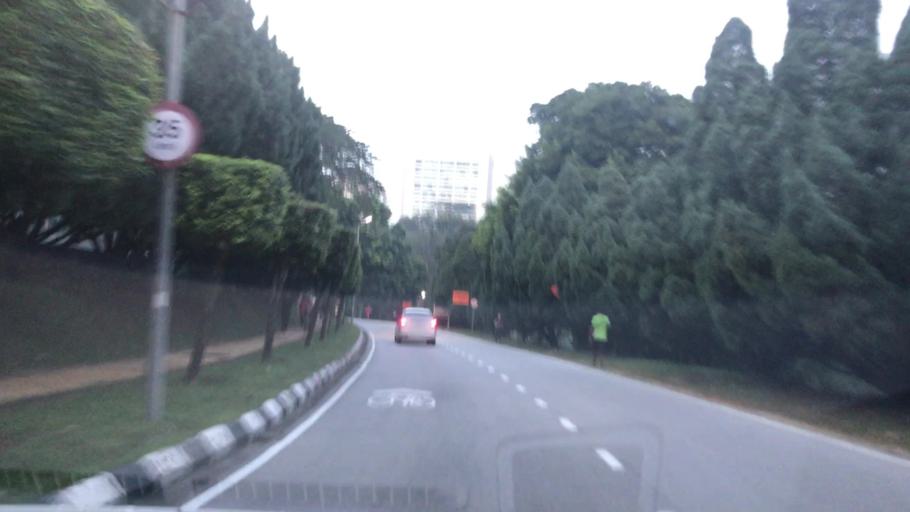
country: MY
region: Kuala Lumpur
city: Kuala Lumpur
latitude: 3.1216
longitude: 101.6588
